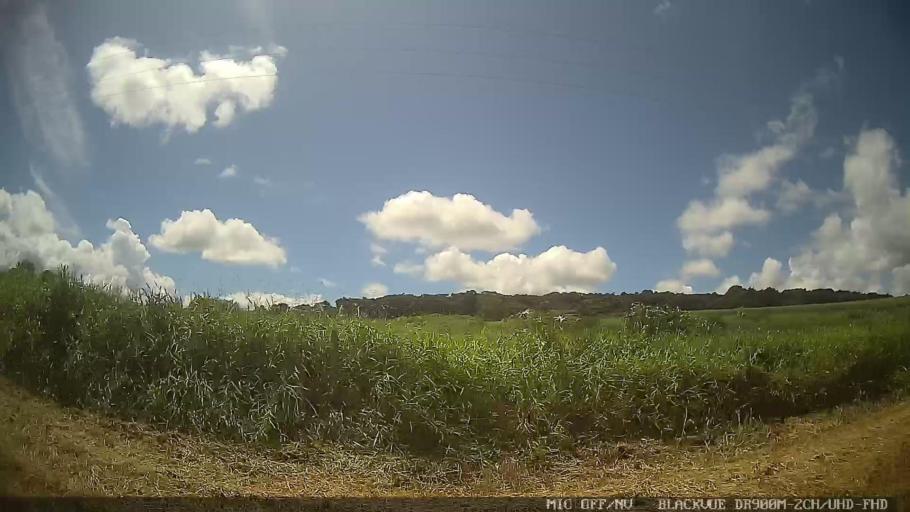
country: BR
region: Sao Paulo
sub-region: Amparo
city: Amparo
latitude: -22.8239
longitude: -46.6994
